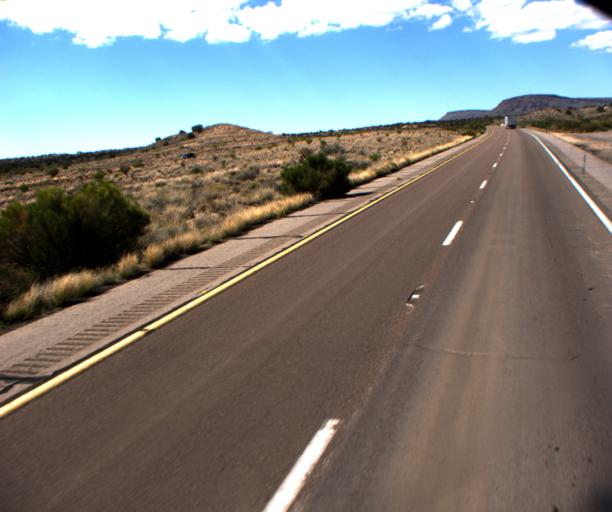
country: US
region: Arizona
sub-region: Mohave County
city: New Kingman-Butler
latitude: 35.1247
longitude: -113.6663
